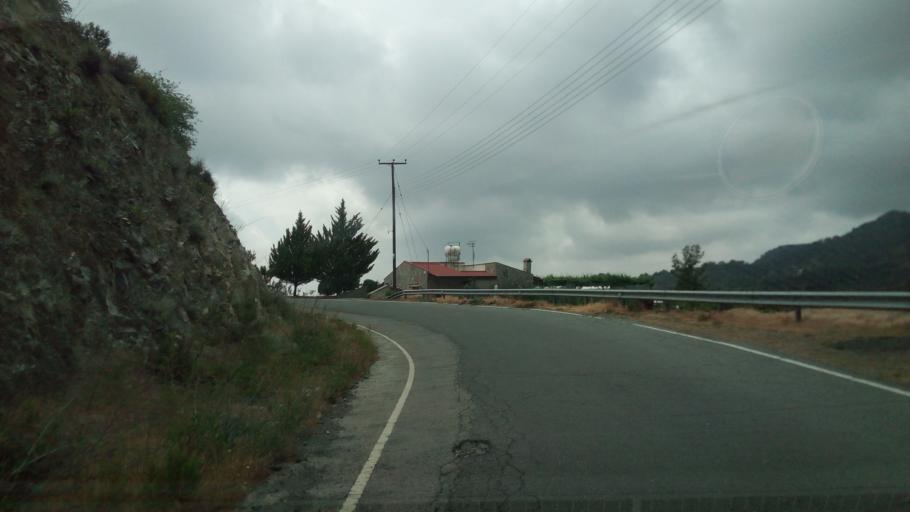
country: CY
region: Limassol
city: Pelendri
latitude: 34.9003
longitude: 32.9929
